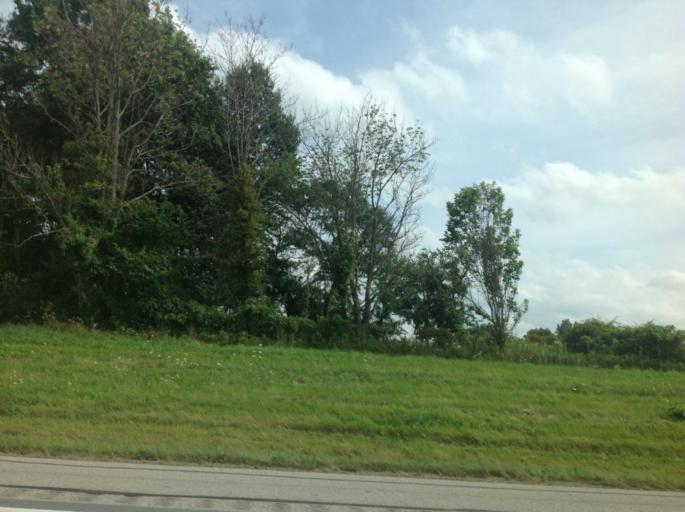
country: US
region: Ohio
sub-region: Ashland County
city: Ashland
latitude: 40.8774
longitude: -82.2061
